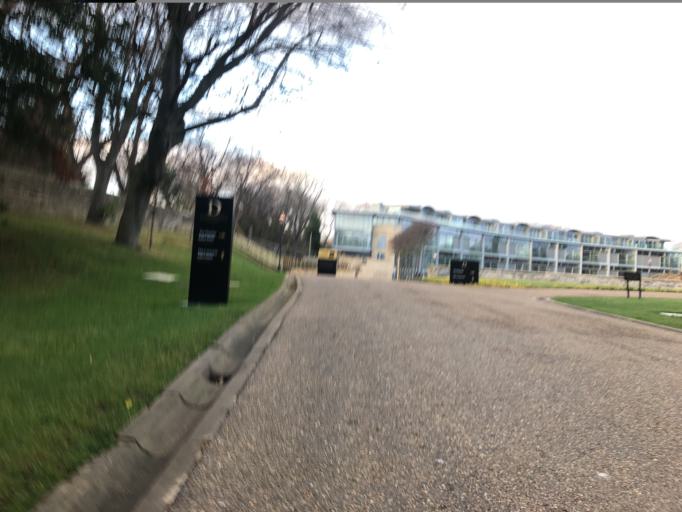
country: GB
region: Scotland
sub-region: Edinburgh
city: Edinburgh
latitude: 55.9468
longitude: -3.2276
